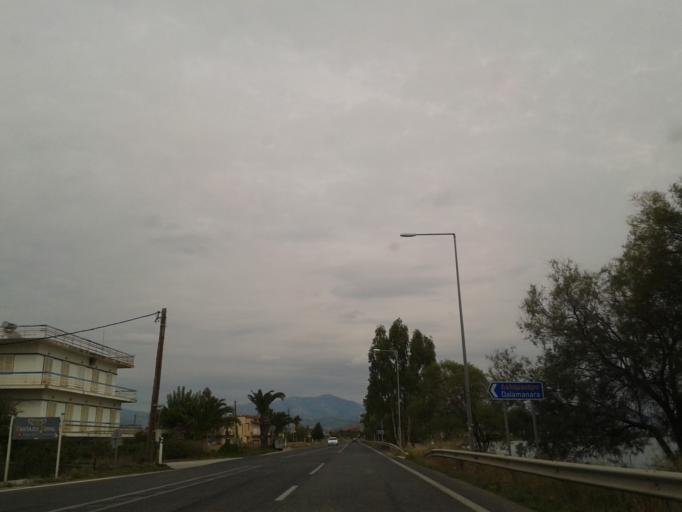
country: GR
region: Peloponnese
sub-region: Nomos Argolidos
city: Nea Kios
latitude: 37.5904
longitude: 22.7661
